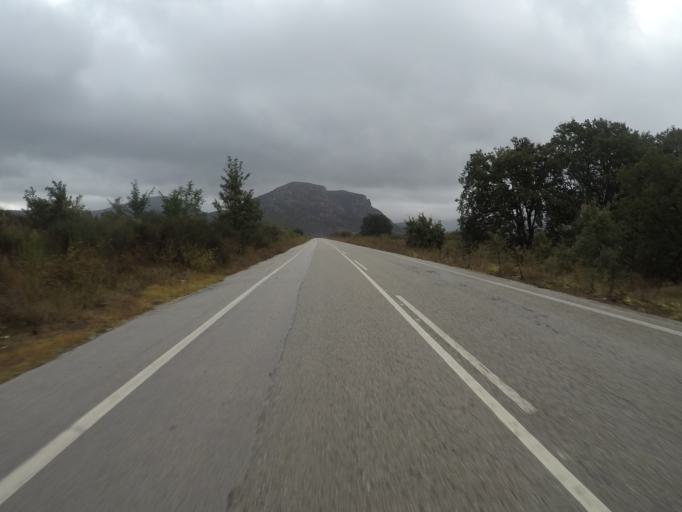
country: GR
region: Peloponnese
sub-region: Nomos Arkadias
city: Tripoli
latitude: 37.5855
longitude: 22.4252
